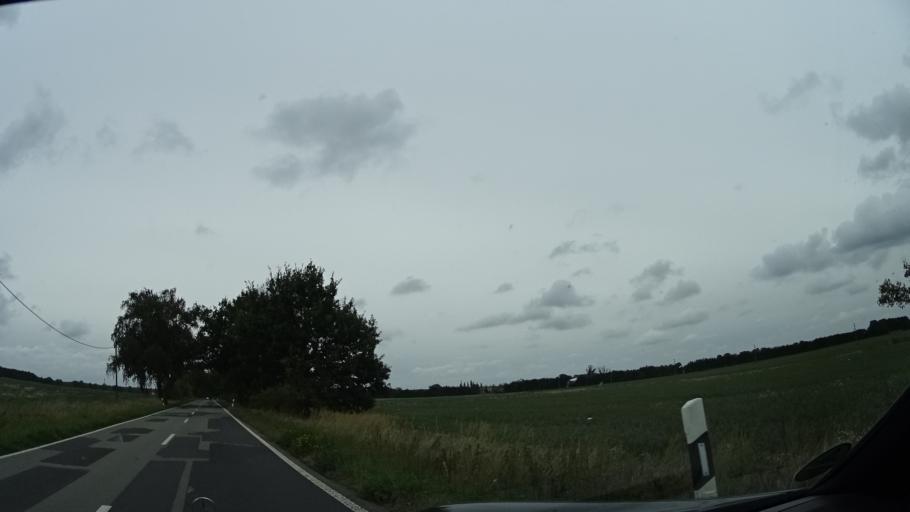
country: DE
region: Brandenburg
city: Walsleben
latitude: 52.9470
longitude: 12.7045
